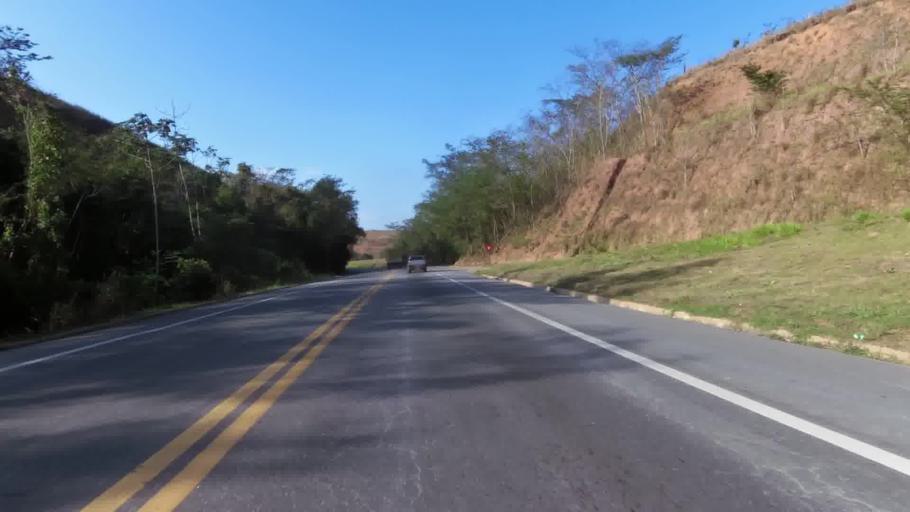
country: BR
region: Espirito Santo
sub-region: Mimoso Do Sul
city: Mimoso do Sul
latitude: -21.1906
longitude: -41.2947
